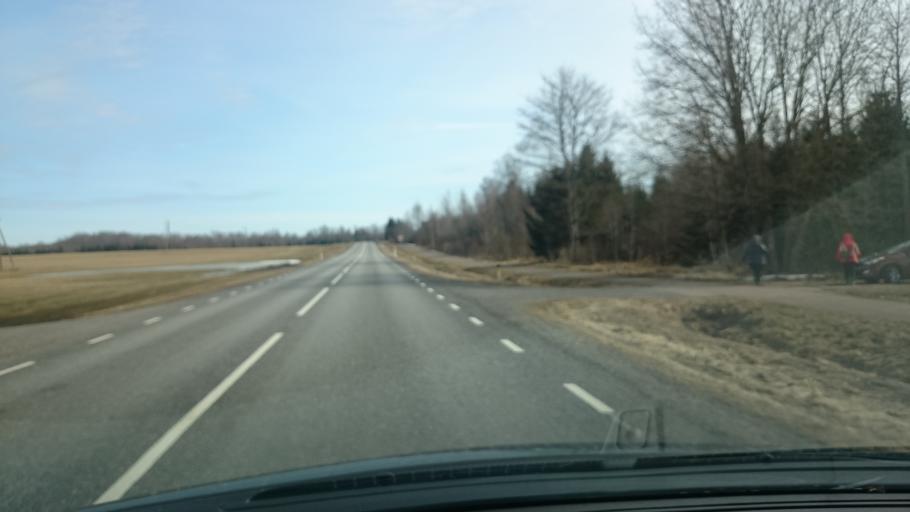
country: EE
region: Jaervamaa
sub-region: Paide linn
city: Paide
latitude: 58.8864
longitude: 25.5089
